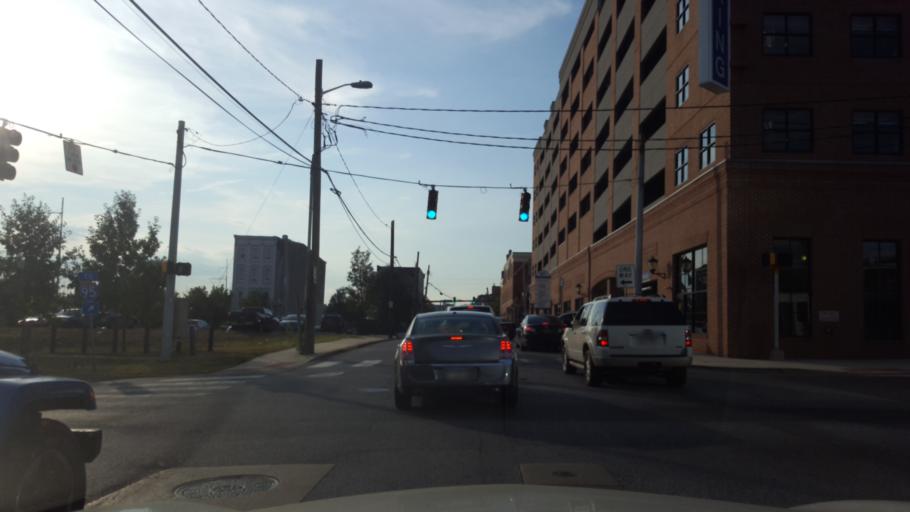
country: US
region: Delaware
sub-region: New Castle County
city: Wilmington
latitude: 39.7384
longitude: -75.5514
